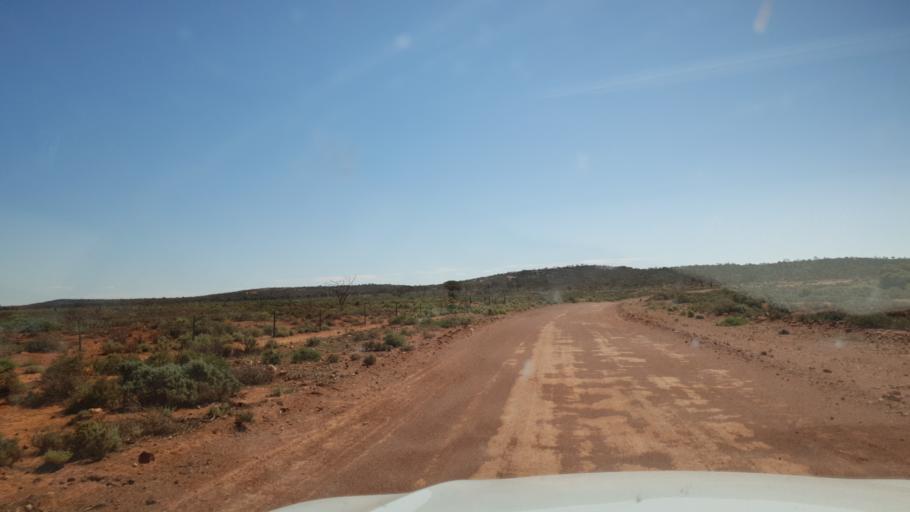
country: AU
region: South Australia
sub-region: Kimba
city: Caralue
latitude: -32.5057
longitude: 136.4817
